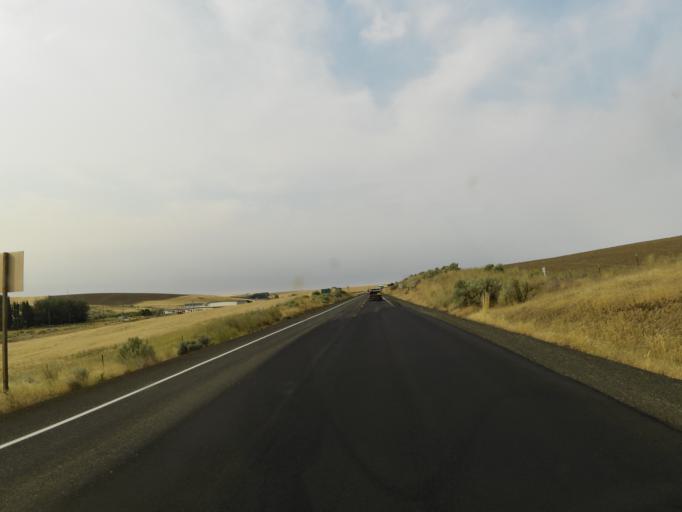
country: US
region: Oregon
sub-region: Sherman County
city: Moro
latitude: 45.4785
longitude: -120.7390
